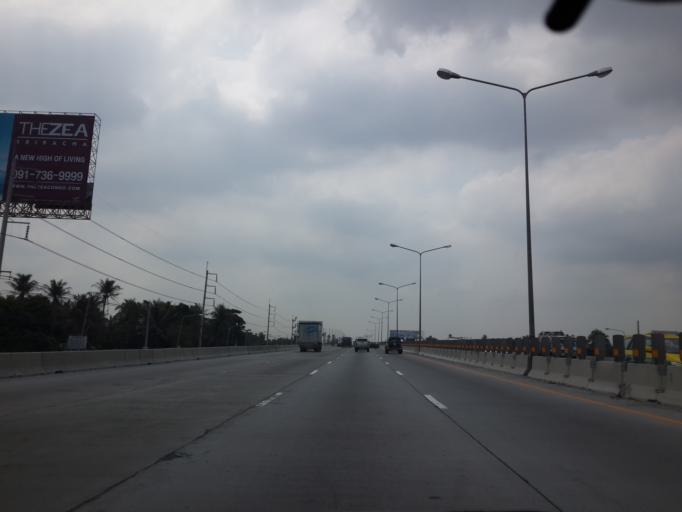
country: TH
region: Chon Buri
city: Si Racha
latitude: 13.1838
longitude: 100.9964
